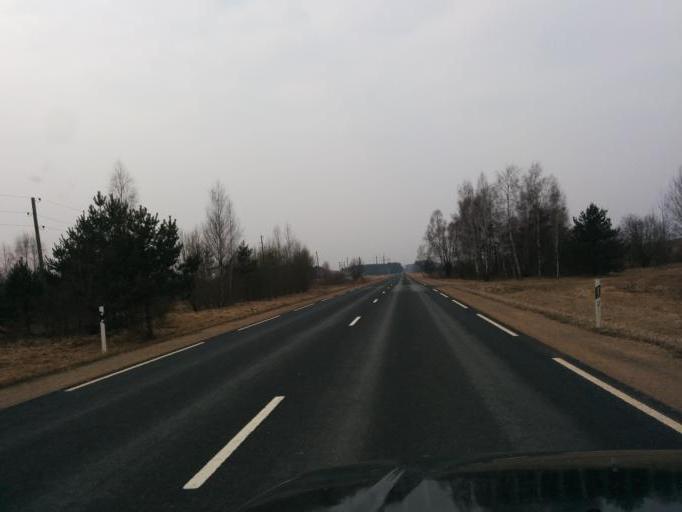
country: LV
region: Salaspils
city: Salaspils
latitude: 56.8231
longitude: 24.3077
